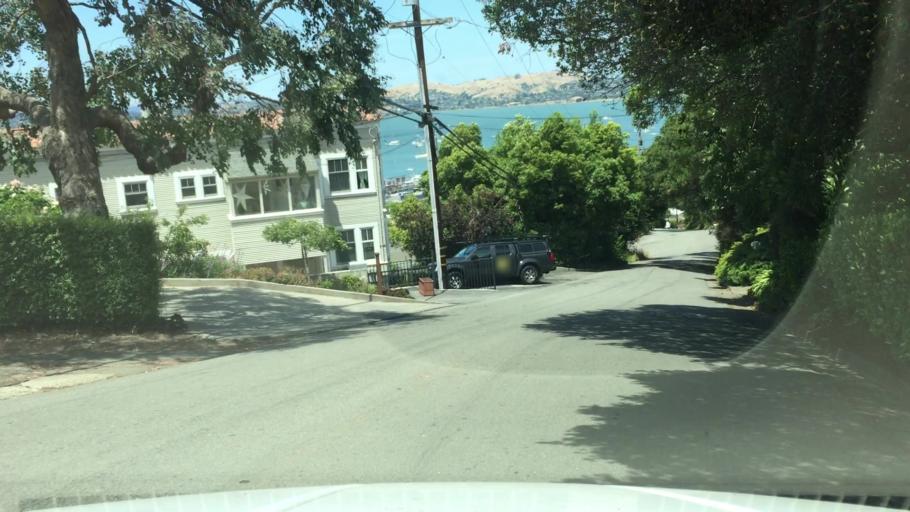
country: US
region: California
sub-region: Marin County
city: Sausalito
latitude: 37.8557
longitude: -122.4844
